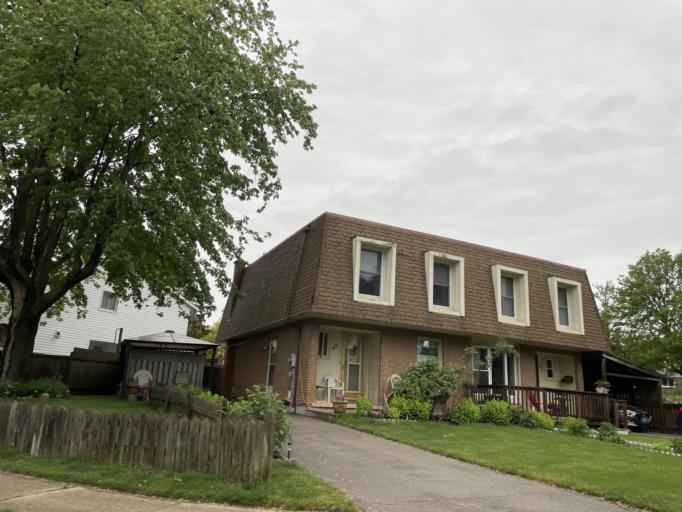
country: CA
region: Ontario
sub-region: Wellington County
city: Guelph
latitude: 43.5565
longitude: -80.2808
